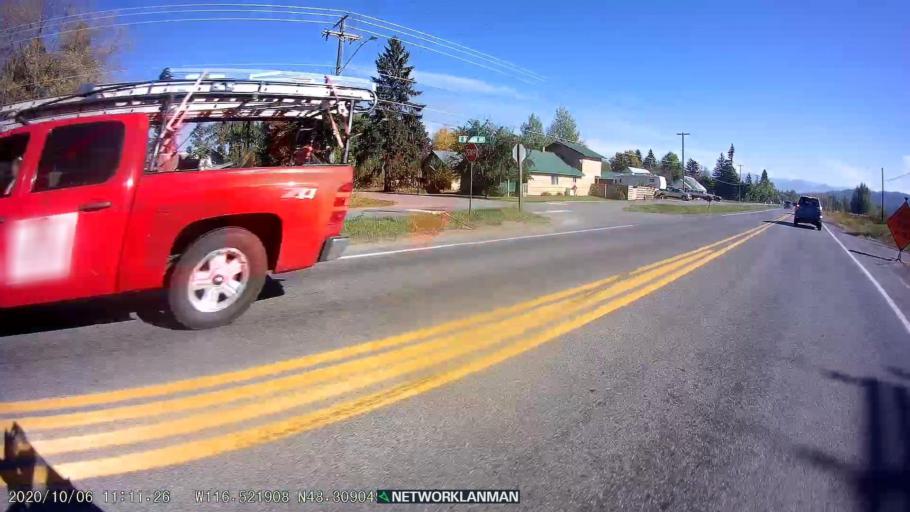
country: US
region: Idaho
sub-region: Bonner County
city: Ponderay
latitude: 48.3090
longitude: -116.5219
